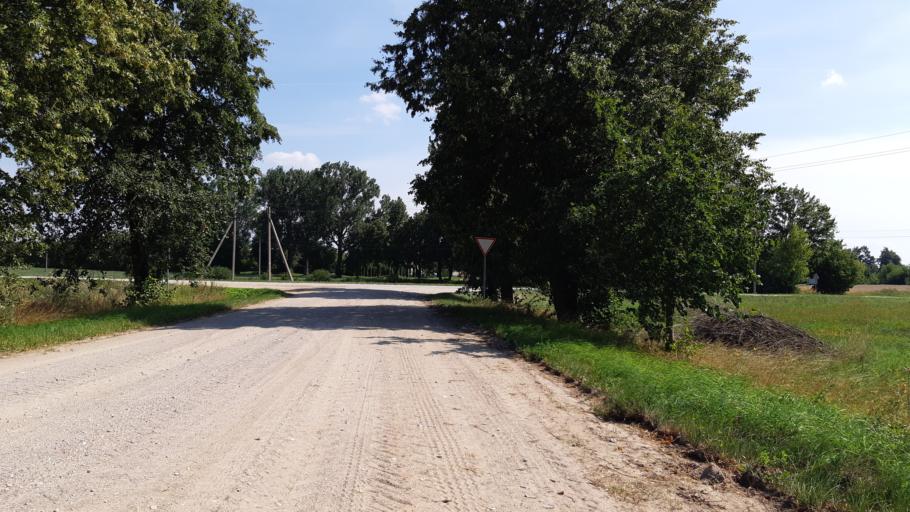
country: LT
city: Virbalis
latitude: 54.6340
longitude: 22.8267
